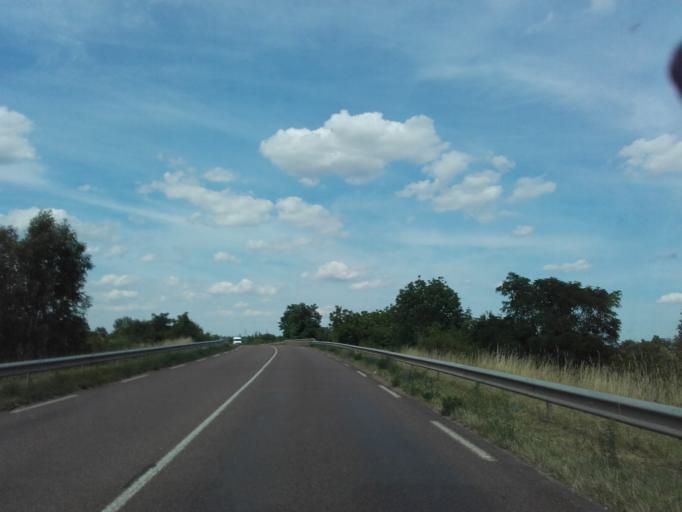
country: FR
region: Bourgogne
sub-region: Departement de Saone-et-Loire
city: Chagny
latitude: 46.9145
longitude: 4.7250
